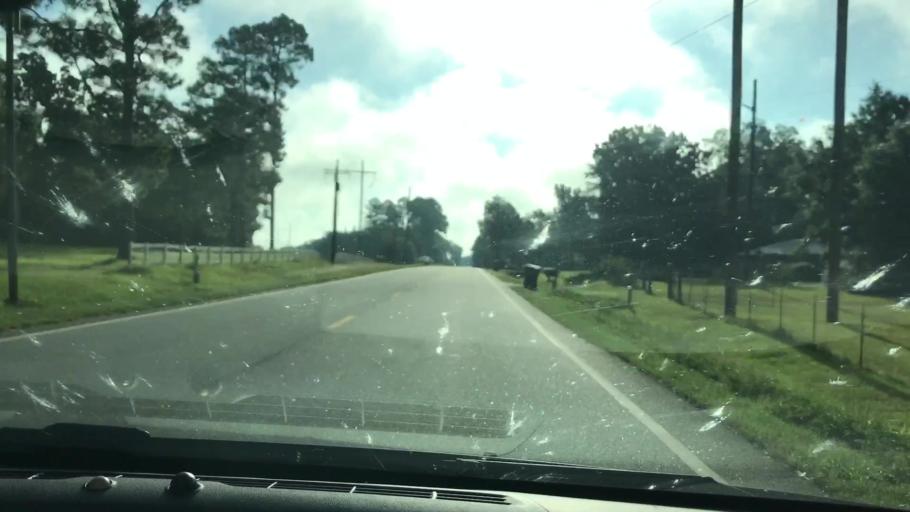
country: US
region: Georgia
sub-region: Terrell County
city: Dawson
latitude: 31.7703
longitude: -84.5257
